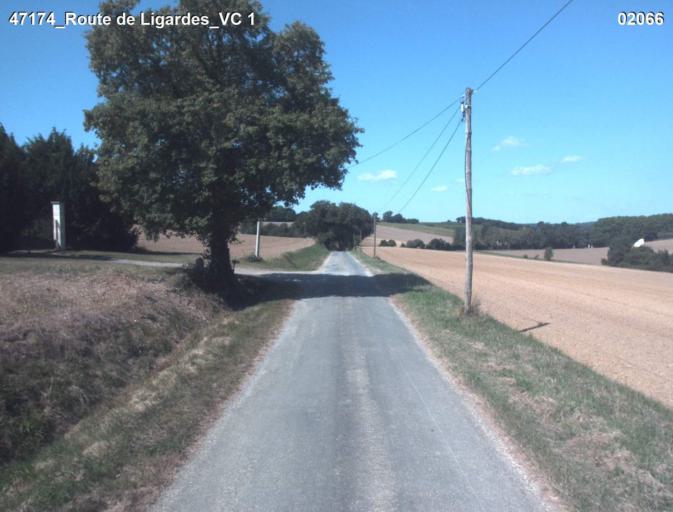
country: FR
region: Midi-Pyrenees
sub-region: Departement du Gers
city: Condom
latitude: 44.0343
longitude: 0.3955
